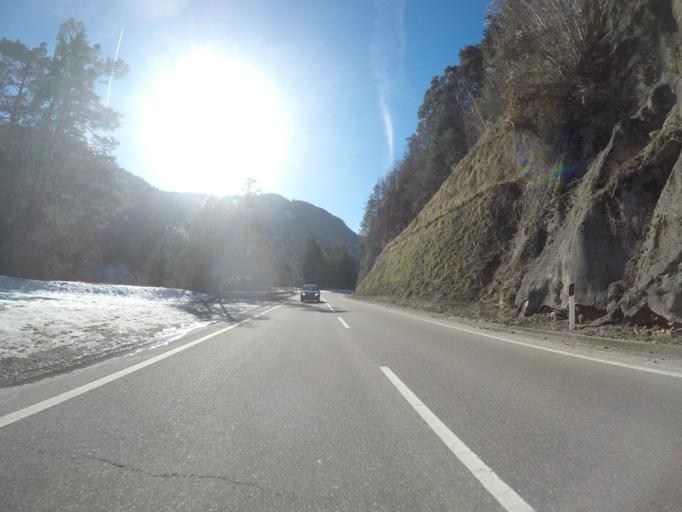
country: IT
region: Trentino-Alto Adige
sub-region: Bolzano
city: Anterivo
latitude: 46.2651
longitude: 11.3910
